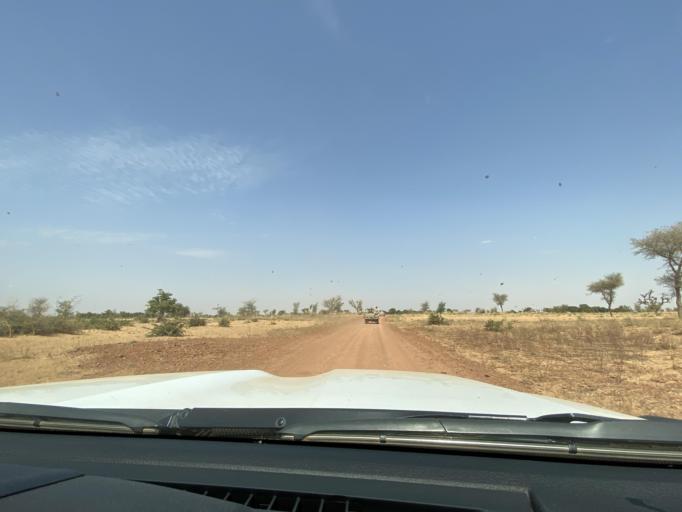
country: NE
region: Dosso
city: Birnin Gaoure
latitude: 13.2354
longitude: 2.8679
